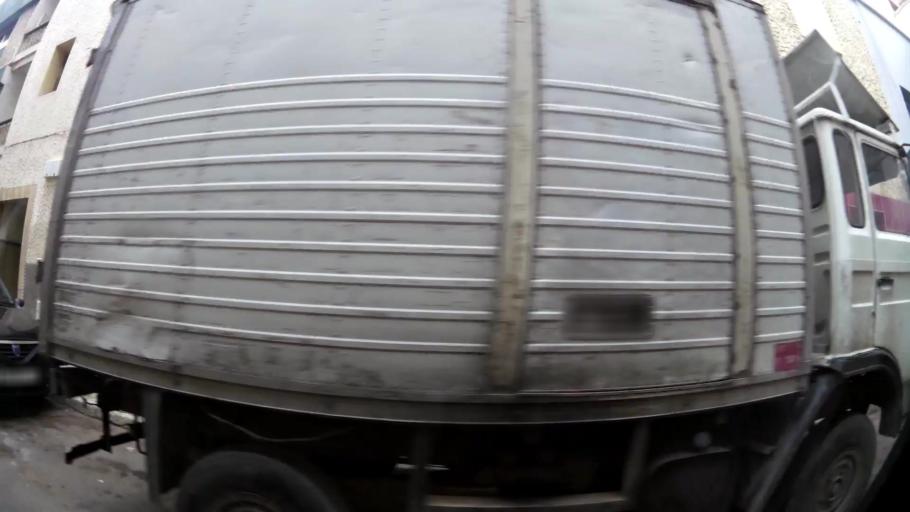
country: MA
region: Grand Casablanca
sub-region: Casablanca
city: Casablanca
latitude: 33.5707
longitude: -7.6479
